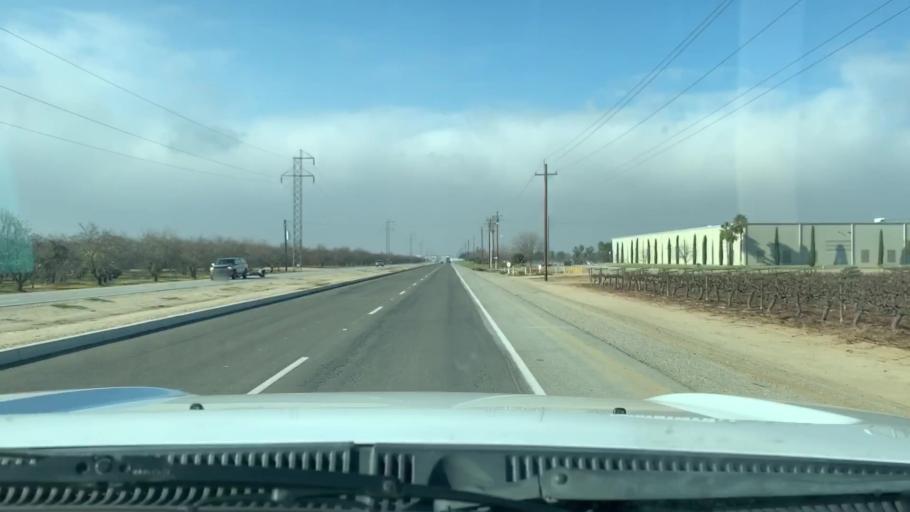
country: US
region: California
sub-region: Kern County
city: Rosedale
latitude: 35.4418
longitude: -119.1792
